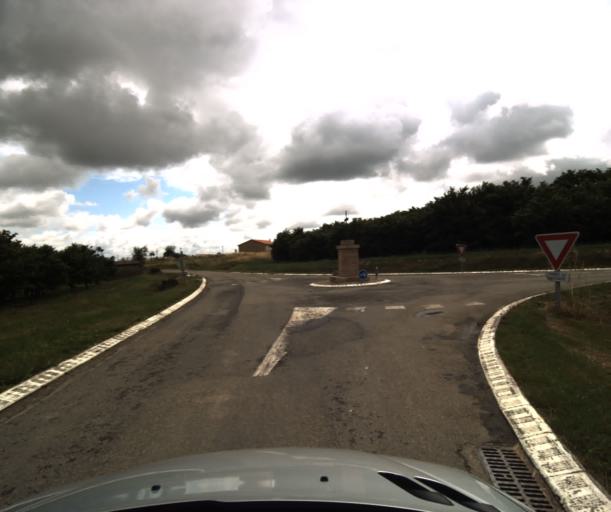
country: FR
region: Midi-Pyrenees
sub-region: Departement du Tarn-et-Garonne
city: Lavit
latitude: 43.9635
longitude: 0.9184
